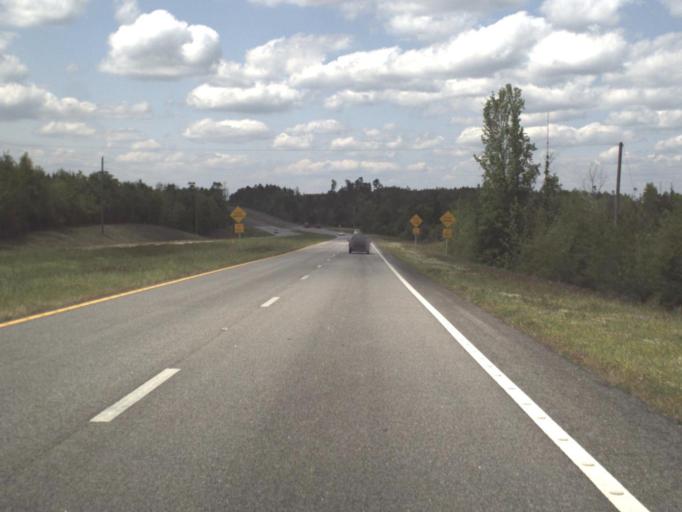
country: US
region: Florida
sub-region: Escambia County
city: Molino
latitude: 30.7915
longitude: -87.3336
